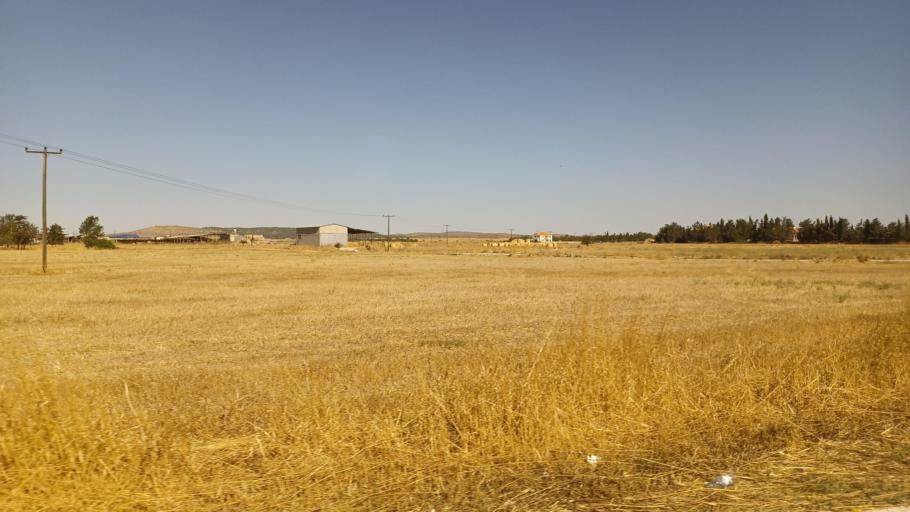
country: CY
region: Larnaka
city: Pergamos
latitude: 35.0328
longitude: 33.7054
